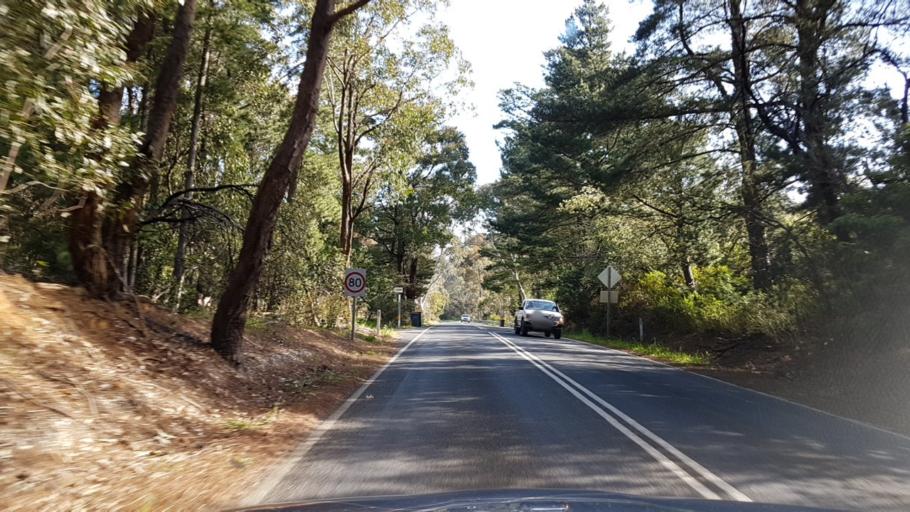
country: AU
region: South Australia
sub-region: Adelaide Hills
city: Lobethal
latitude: -34.8794
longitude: 138.8913
